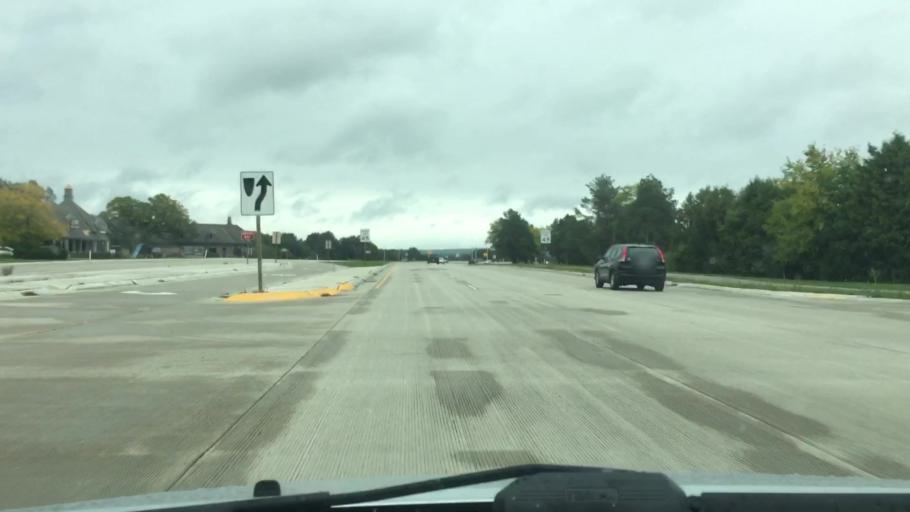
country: US
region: Wisconsin
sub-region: Waukesha County
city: Oconomowoc
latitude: 43.0903
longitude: -88.4750
